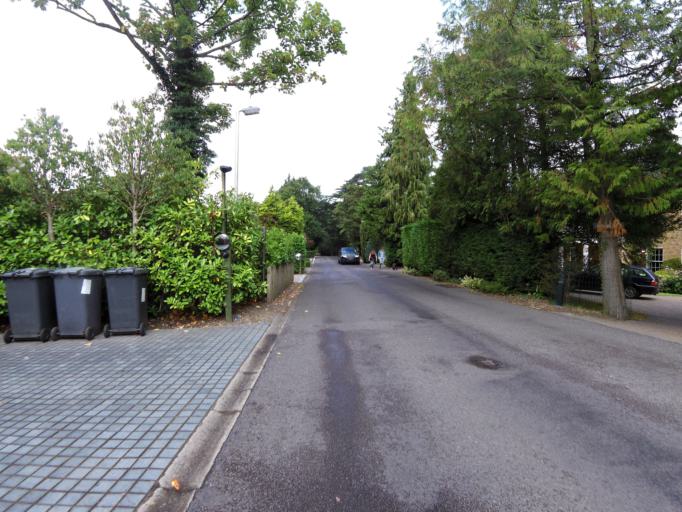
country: GB
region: England
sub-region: Hertfordshire
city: Radlett
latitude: 51.6876
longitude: -0.3122
